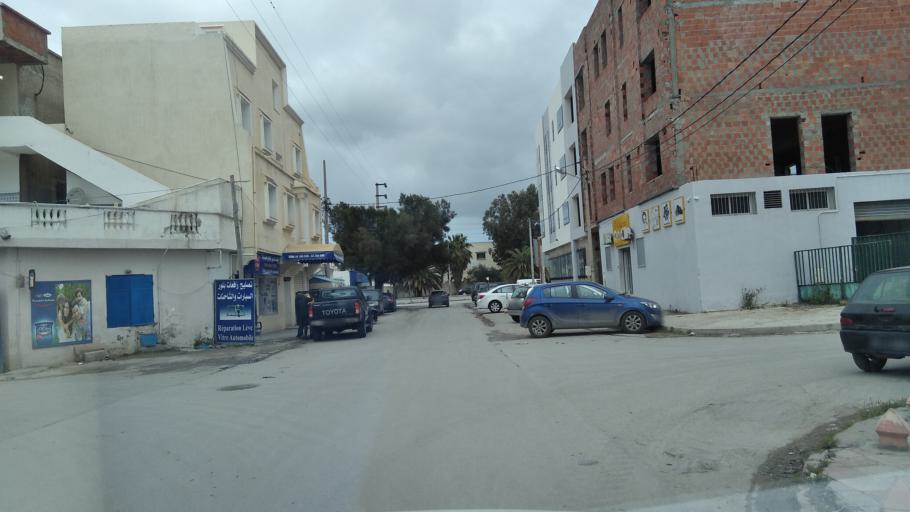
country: TN
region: Bin 'Arus
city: Ben Arous
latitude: 36.7625
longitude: 10.2280
